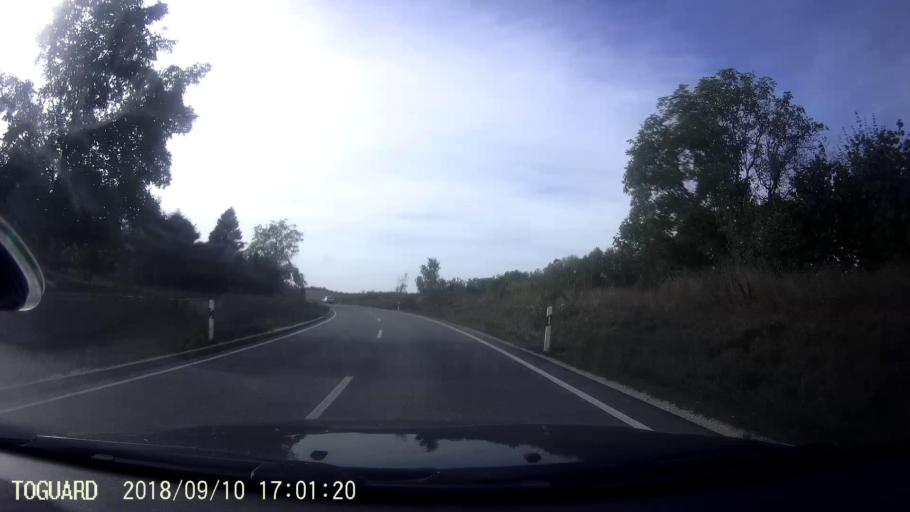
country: CH
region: Thurgau
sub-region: Kreuzlingen District
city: Gottlieben
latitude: 47.6937
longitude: 9.1357
